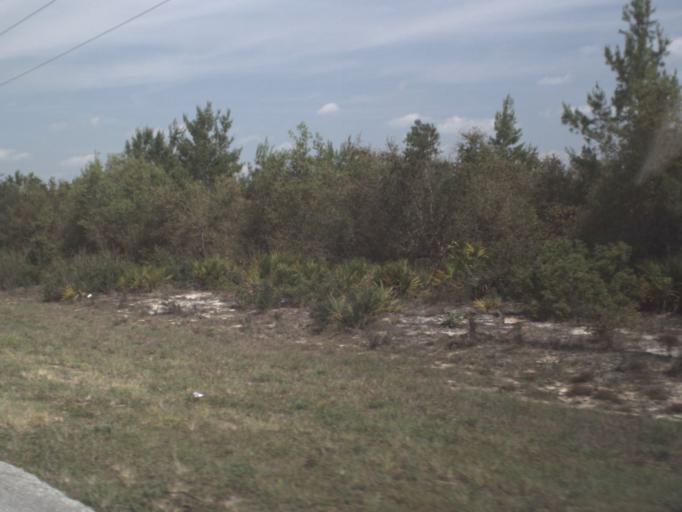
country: US
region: Florida
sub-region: Putnam County
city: Crescent City
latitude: 29.3237
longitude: -81.7030
